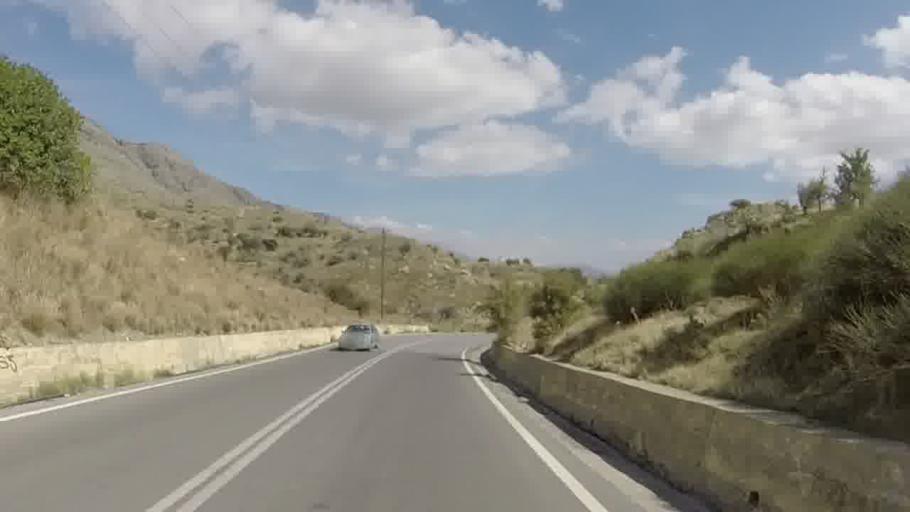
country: GR
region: Crete
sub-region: Nomos Rethymnis
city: Agia Galini
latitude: 35.1484
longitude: 24.6315
